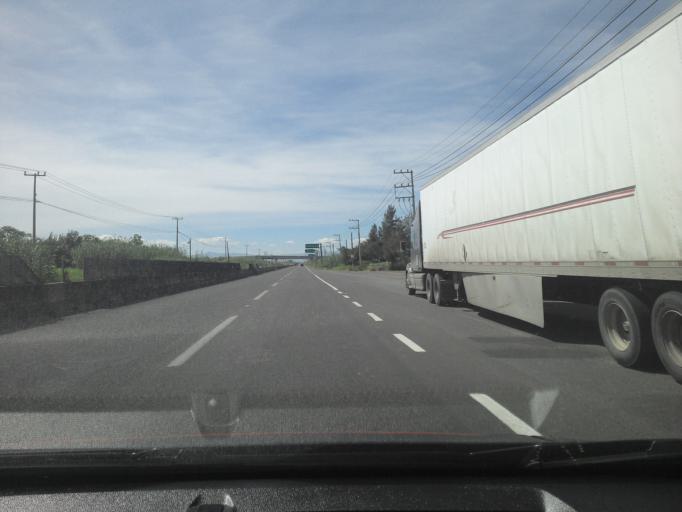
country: MX
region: Jalisco
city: El Refugio
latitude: 20.6608
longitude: -103.7289
